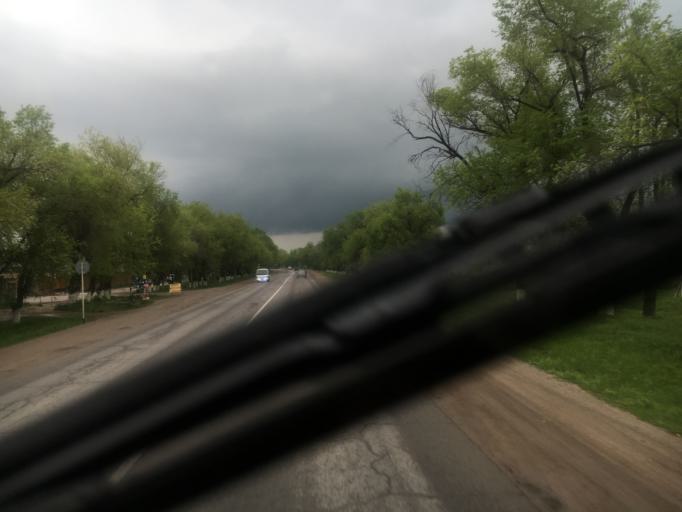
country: KZ
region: Almaty Oblysy
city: Burunday
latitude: 43.2383
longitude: 76.6656
